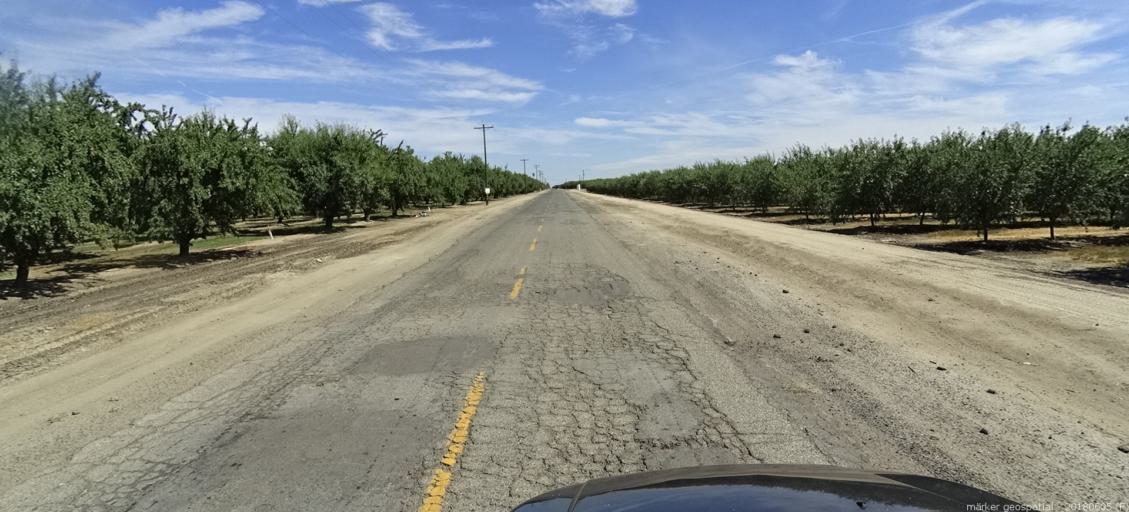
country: US
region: California
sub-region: Madera County
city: Chowchilla
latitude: 37.0950
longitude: -120.3826
